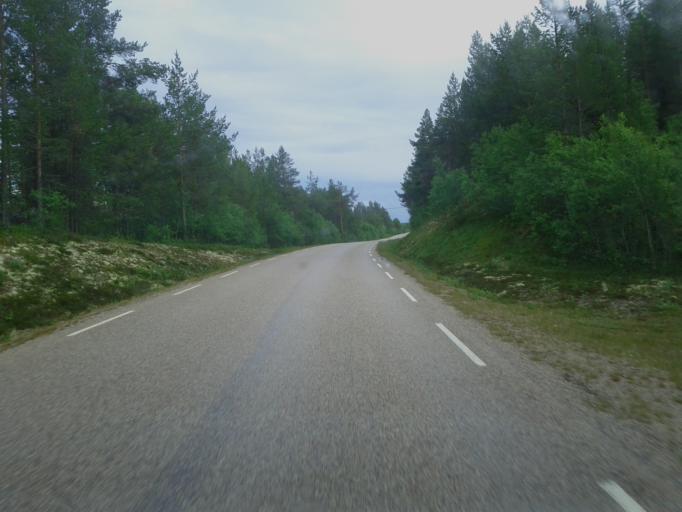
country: NO
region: Hedmark
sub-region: Engerdal
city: Engerdal
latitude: 62.0725
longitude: 11.6756
